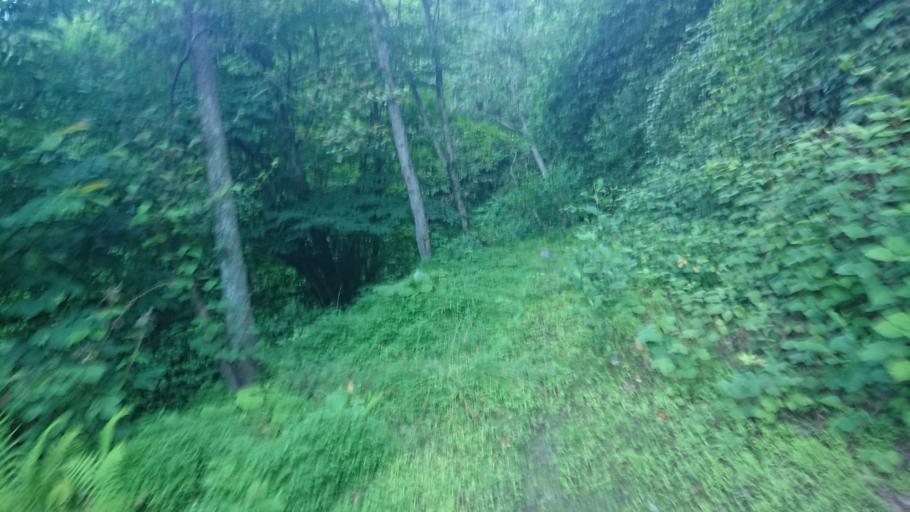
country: TR
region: Rize
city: Rize
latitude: 40.9721
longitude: 40.4952
